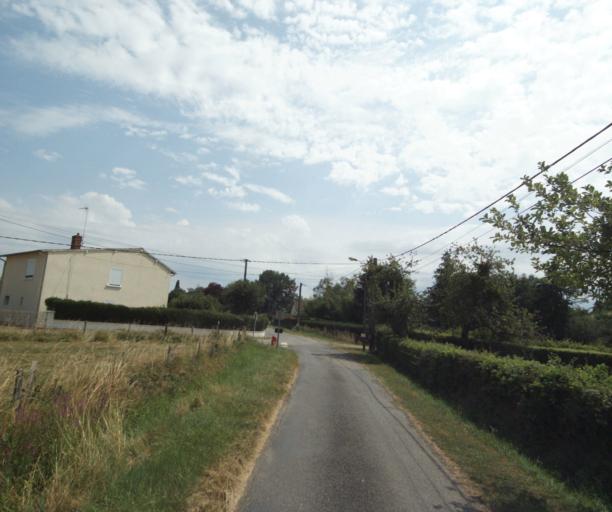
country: FR
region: Bourgogne
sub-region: Departement de Saone-et-Loire
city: Gueugnon
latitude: 46.6126
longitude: 4.0396
